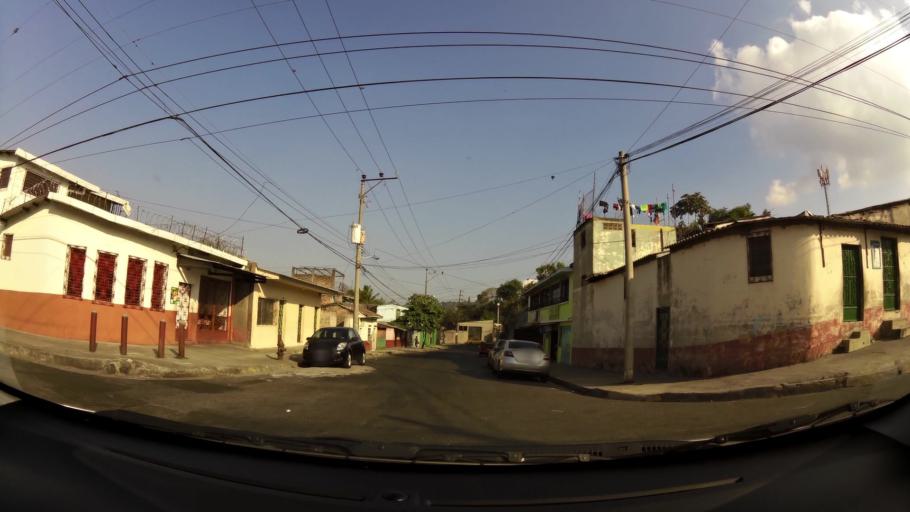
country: SV
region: San Salvador
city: San Salvador
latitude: 13.6971
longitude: -89.1779
